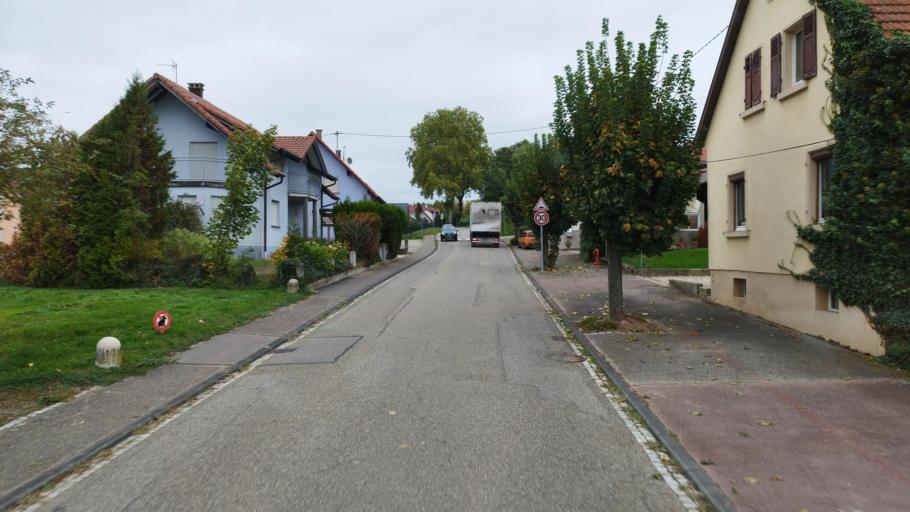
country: DE
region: Rheinland-Pfalz
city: Scheibenhardt
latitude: 48.9562
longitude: 8.1282
